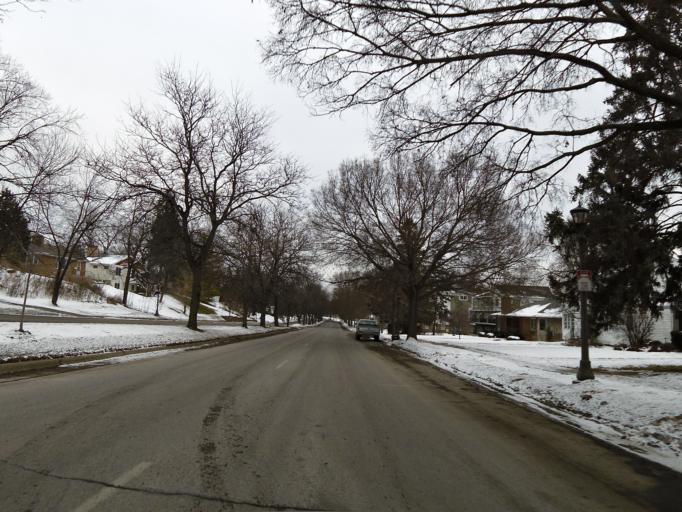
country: US
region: Minnesota
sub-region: Dakota County
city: Mendota Heights
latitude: 44.9122
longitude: -93.1848
